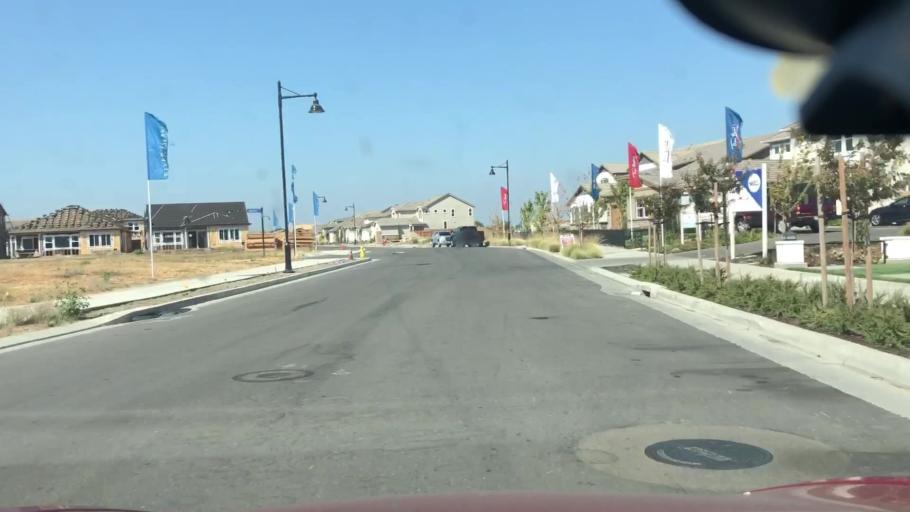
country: US
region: California
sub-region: San Joaquin County
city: Lathrop
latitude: 37.7959
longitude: -121.3279
